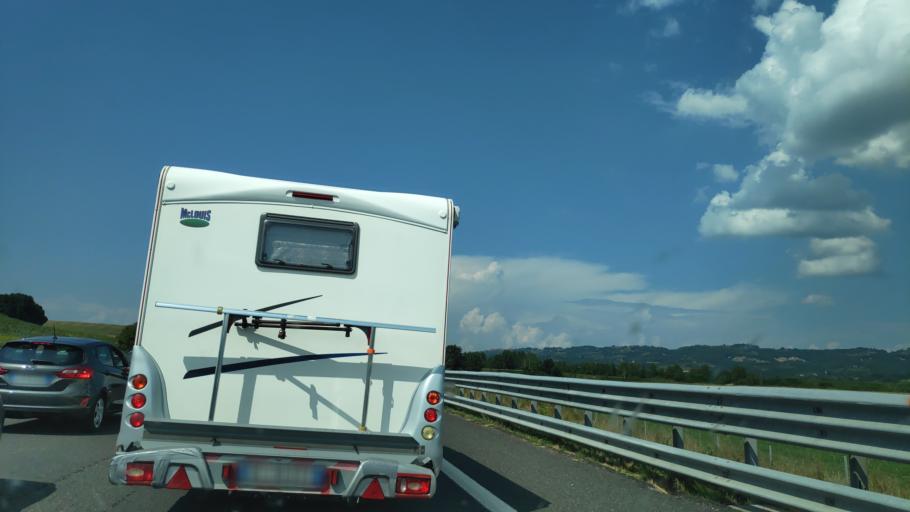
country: IT
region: Umbria
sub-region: Provincia di Terni
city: Fabro
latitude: 42.8886
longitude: 12.0116
